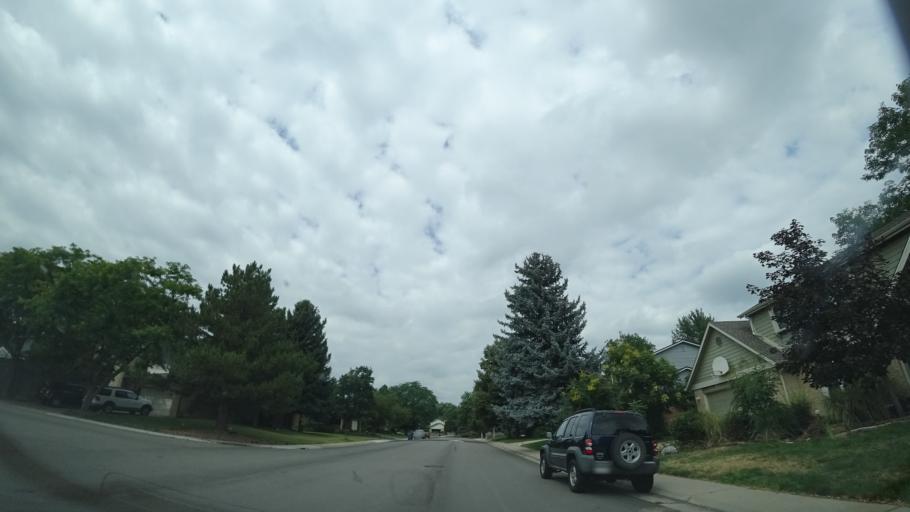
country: US
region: Colorado
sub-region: Jefferson County
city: West Pleasant View
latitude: 39.7209
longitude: -105.1554
